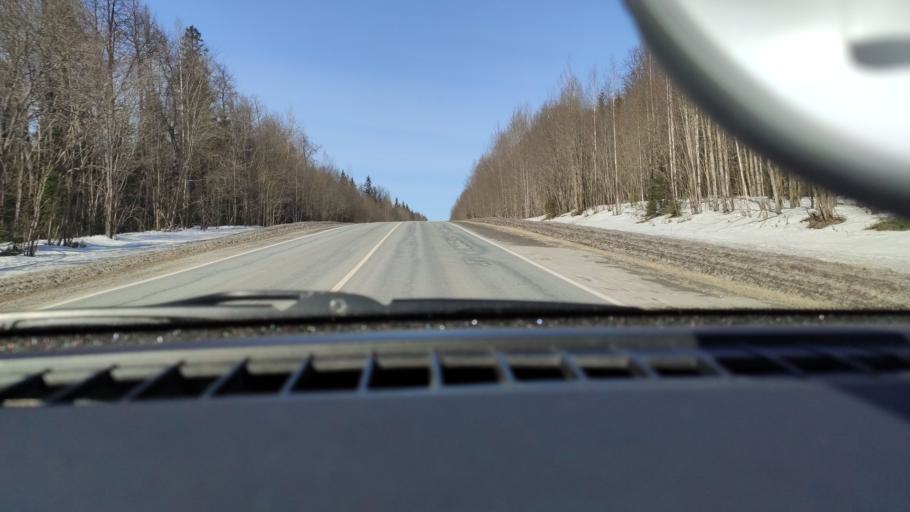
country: RU
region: Perm
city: Perm
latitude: 58.1676
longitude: 56.2382
